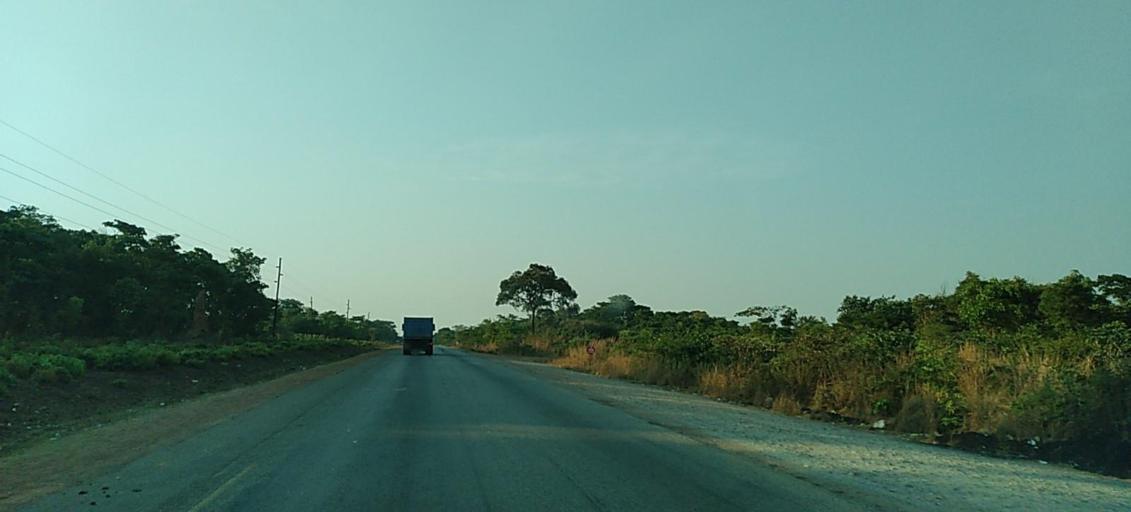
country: ZM
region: Copperbelt
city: Ndola
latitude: -13.1175
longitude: 28.6980
